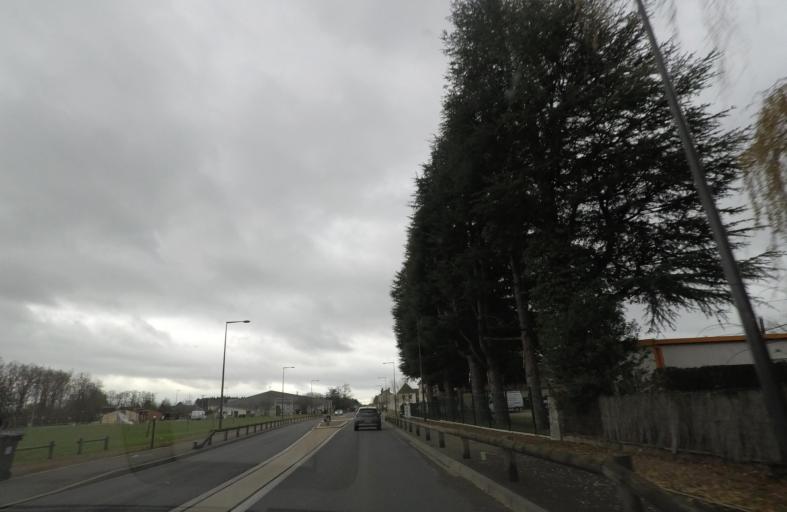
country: FR
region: Centre
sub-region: Departement du Loir-et-Cher
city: Cour-Cheverny
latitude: 47.5134
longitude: 1.4549
